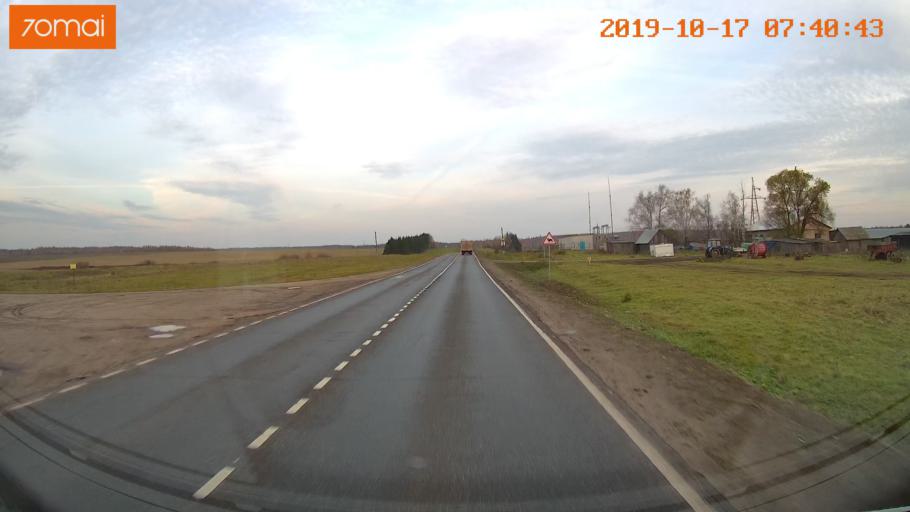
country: RU
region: Vladimir
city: Yur'yev-Pol'skiy
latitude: 56.4761
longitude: 39.8249
